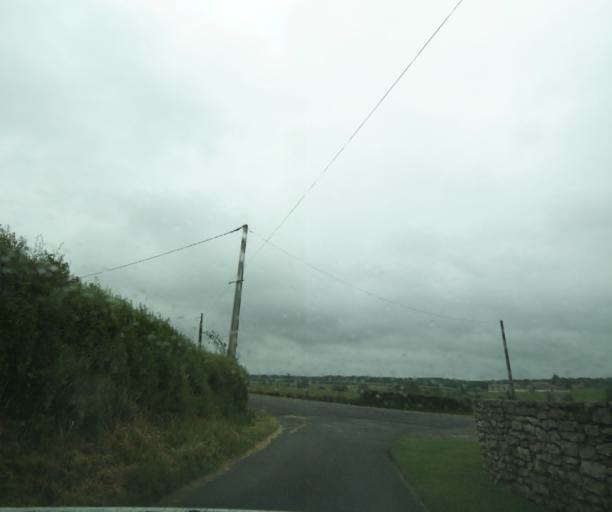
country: FR
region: Bourgogne
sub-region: Departement de Saone-et-Loire
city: Palinges
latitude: 46.4904
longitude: 4.1955
